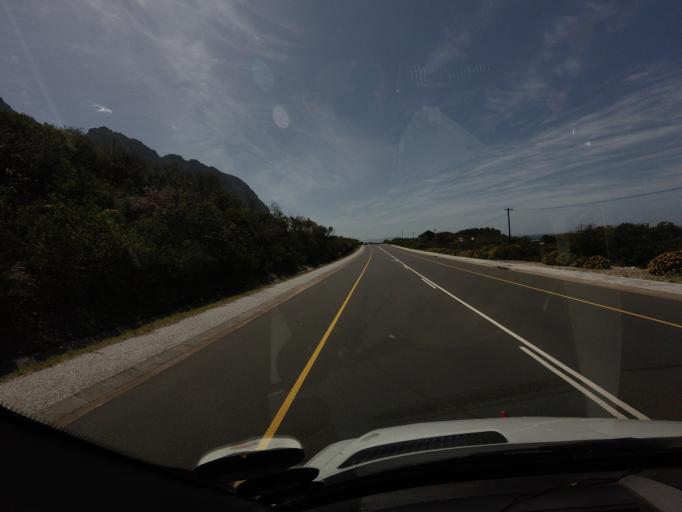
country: ZA
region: Western Cape
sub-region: Overberg District Municipality
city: Grabouw
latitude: -34.3571
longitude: 18.9498
